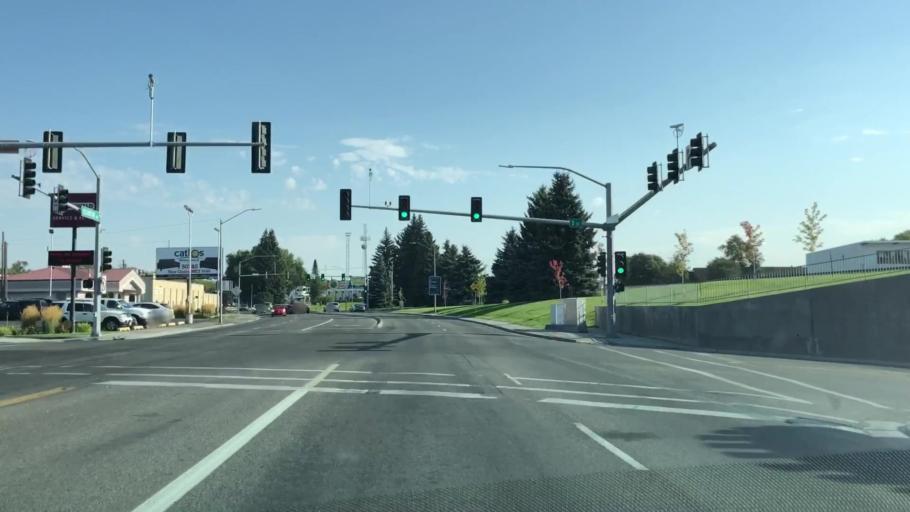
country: US
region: Idaho
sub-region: Bonneville County
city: Idaho Falls
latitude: 43.4940
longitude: -112.0366
